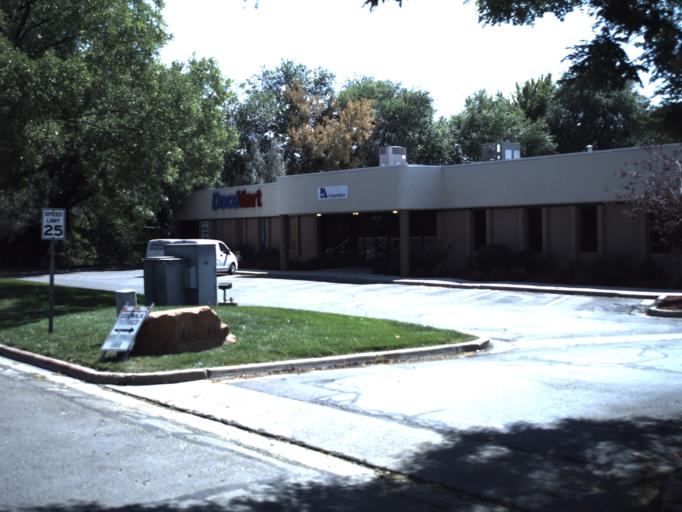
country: US
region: Utah
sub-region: Salt Lake County
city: South Salt Lake
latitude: 40.7227
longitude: -111.9376
